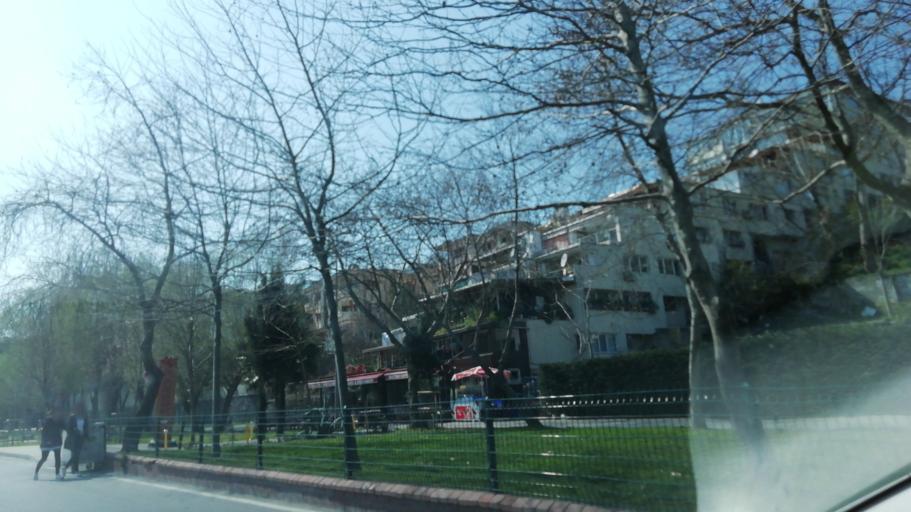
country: TR
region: Istanbul
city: Yakuplu
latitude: 40.9752
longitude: 28.7434
